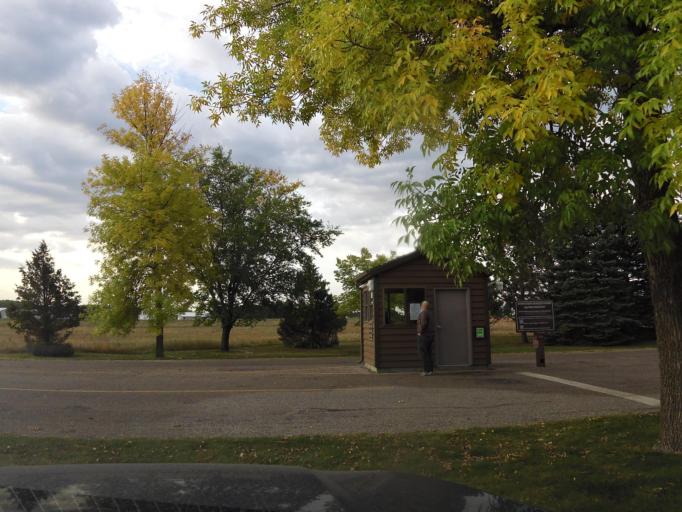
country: US
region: North Dakota
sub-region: Pembina County
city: Cavalier
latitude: 48.7737
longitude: -97.7408
